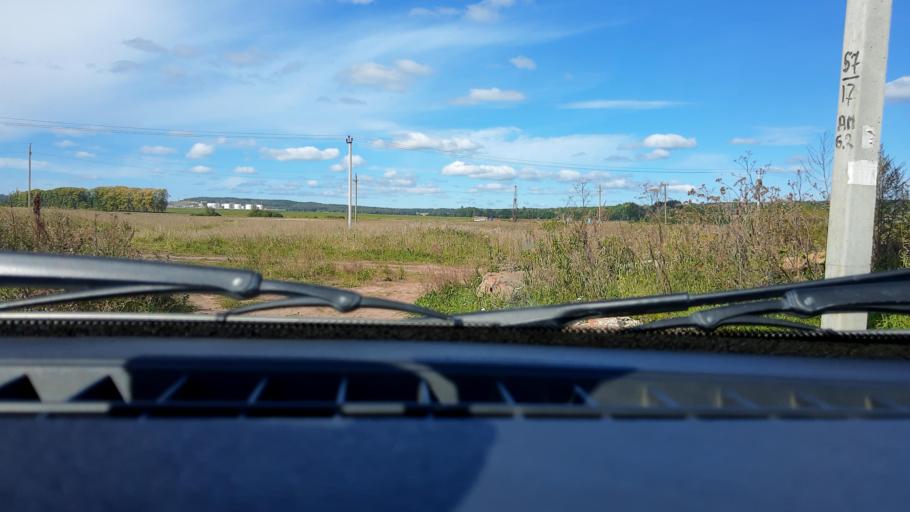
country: RU
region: Bashkortostan
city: Mikhaylovka
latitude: 54.8194
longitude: 55.7898
